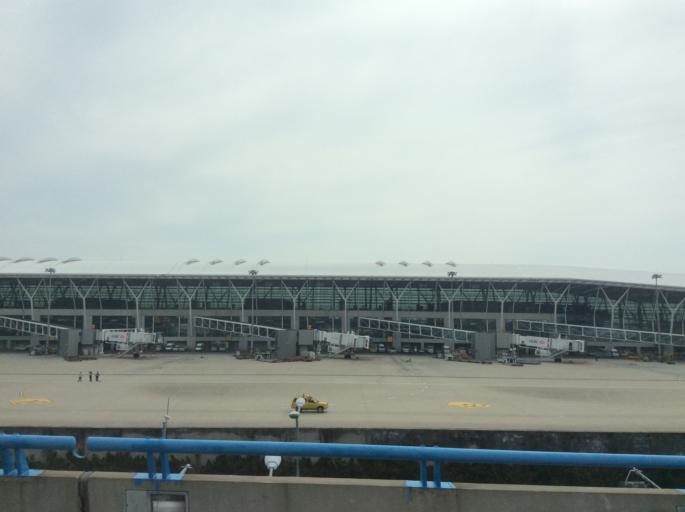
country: CN
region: Shanghai Shi
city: Laogang
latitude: 31.1488
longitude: 121.8054
